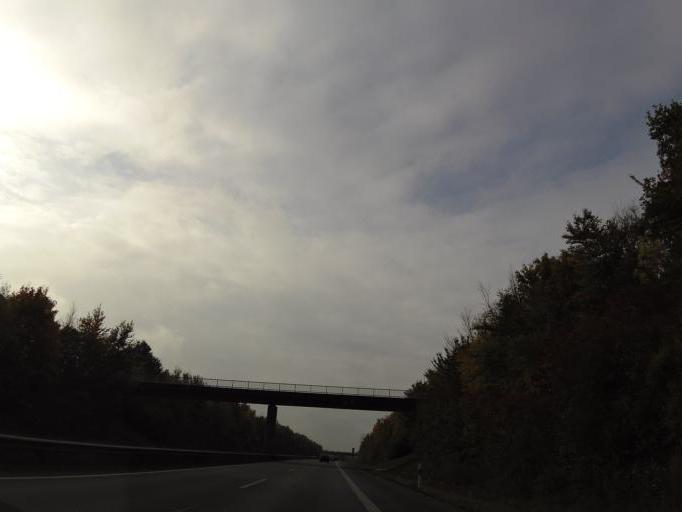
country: DE
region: Rheinland-Pfalz
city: Freimersheim
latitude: 49.7209
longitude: 8.0774
